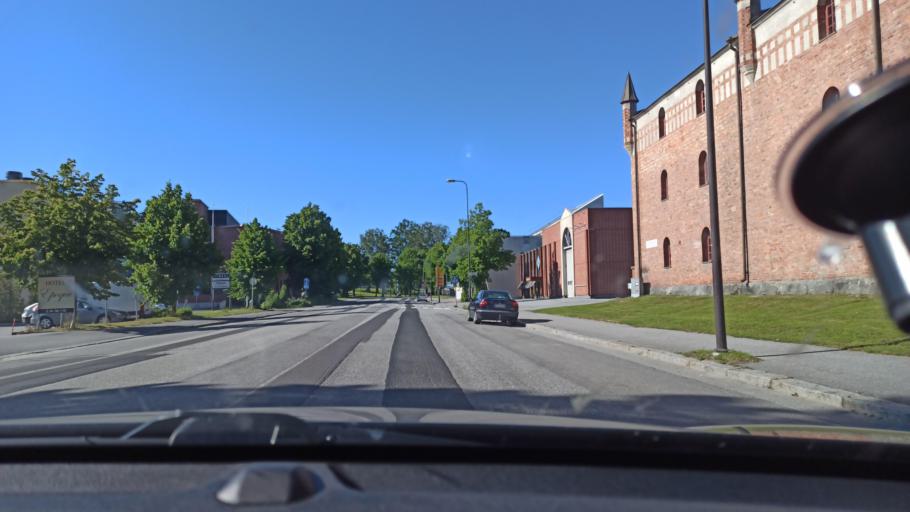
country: FI
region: Ostrobothnia
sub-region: Jakobstadsregionen
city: Jakobstad
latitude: 63.6752
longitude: 22.7119
